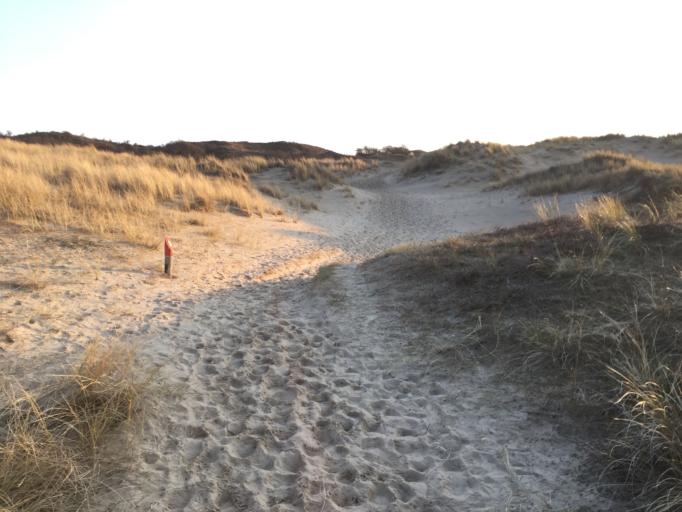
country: NL
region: South Holland
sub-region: Gemeente Katwijk
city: Katwijk aan Zee
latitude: 52.1749
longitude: 4.3726
